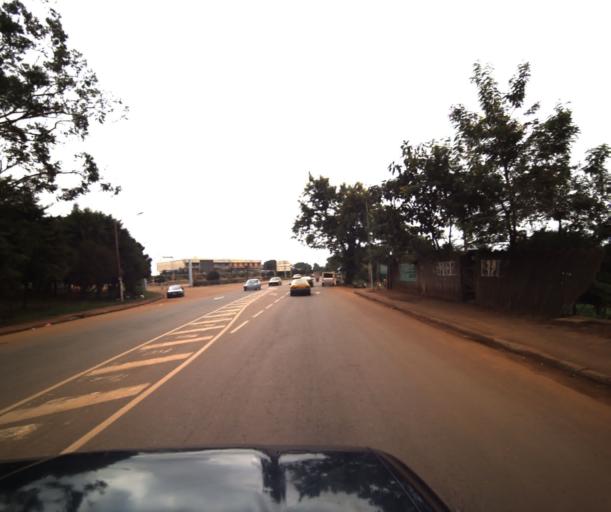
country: CM
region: Centre
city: Yaounde
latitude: 3.8352
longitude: 11.5189
